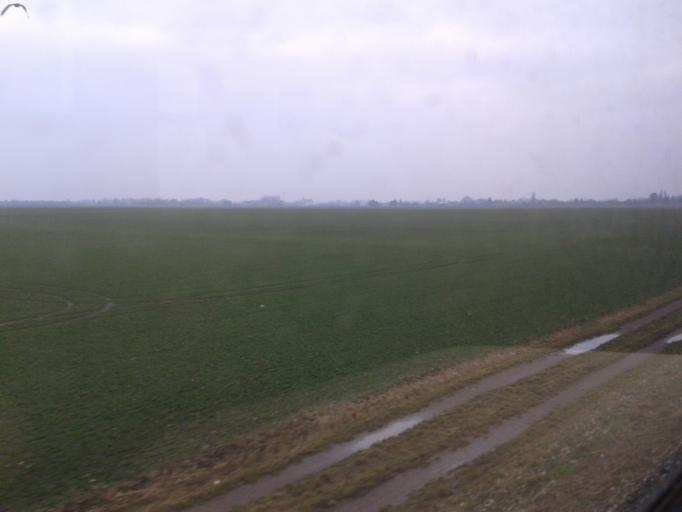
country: CZ
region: Olomoucky
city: Prikazy
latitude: 49.6347
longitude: 17.1270
